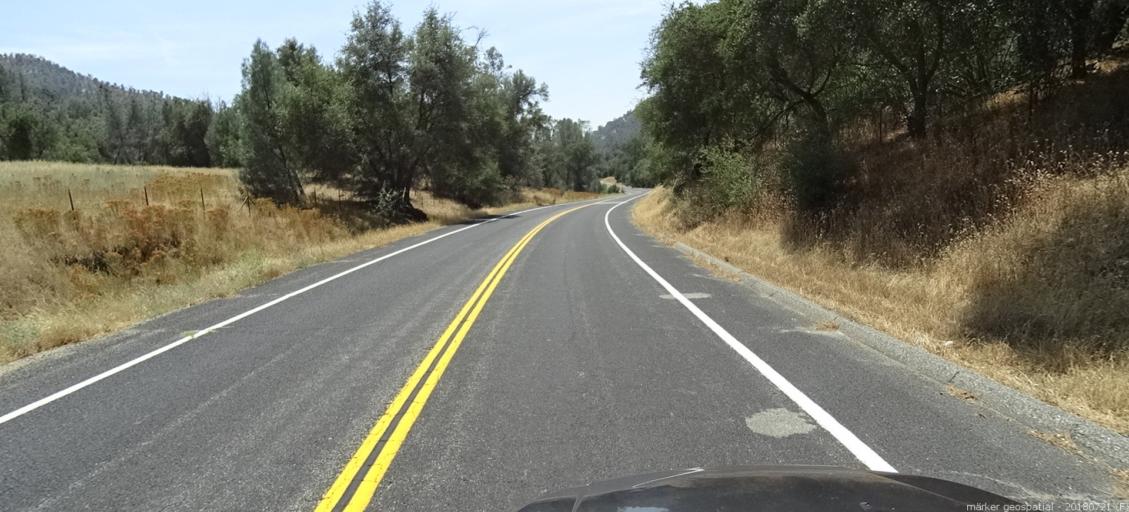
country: US
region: California
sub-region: Madera County
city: Coarsegold
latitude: 37.1899
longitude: -119.6194
